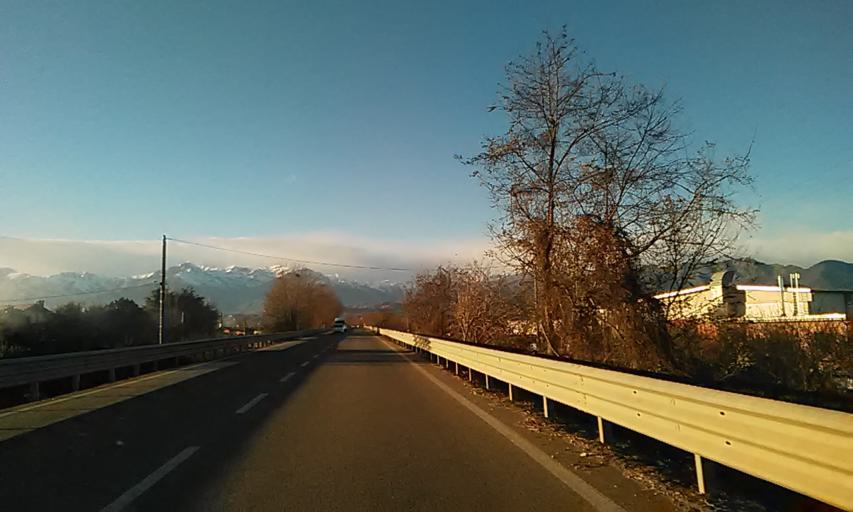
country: IT
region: Piedmont
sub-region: Provincia di Biella
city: Cerreto Castello
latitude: 45.5452
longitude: 8.1769
